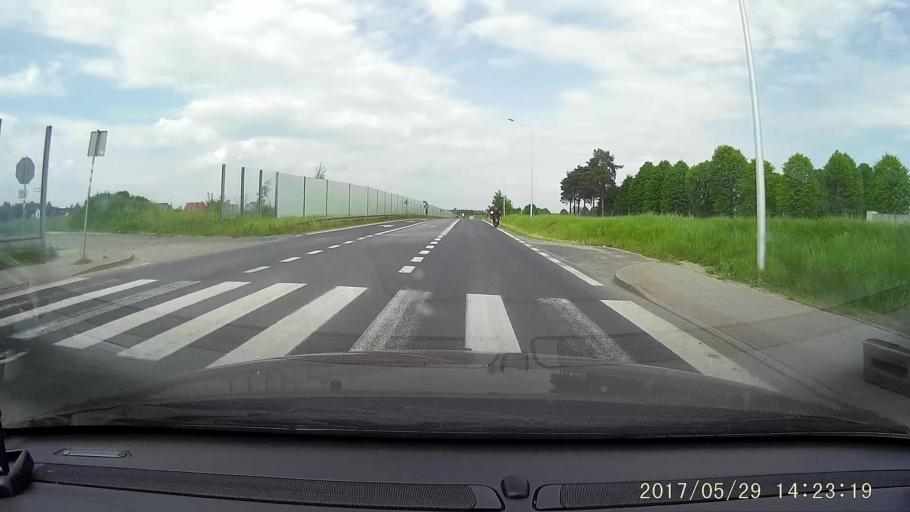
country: PL
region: Lower Silesian Voivodeship
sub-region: Powiat zgorzelecki
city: Zgorzelec
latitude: 51.1364
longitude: 15.0289
